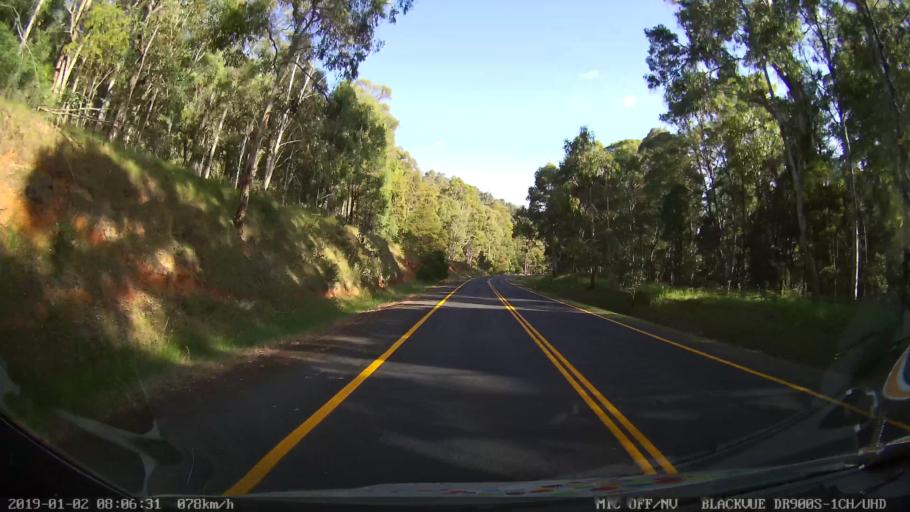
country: AU
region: New South Wales
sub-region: Tumut Shire
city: Tumut
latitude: -35.6391
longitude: 148.3869
